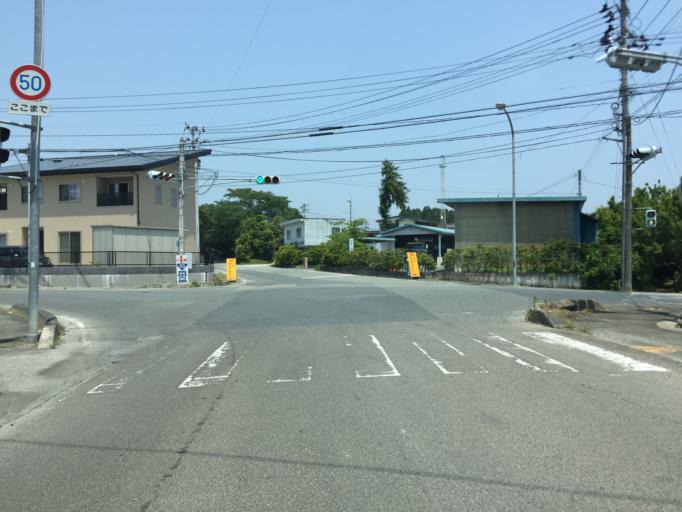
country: JP
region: Miyagi
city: Marumori
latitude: 37.8416
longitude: 140.8931
